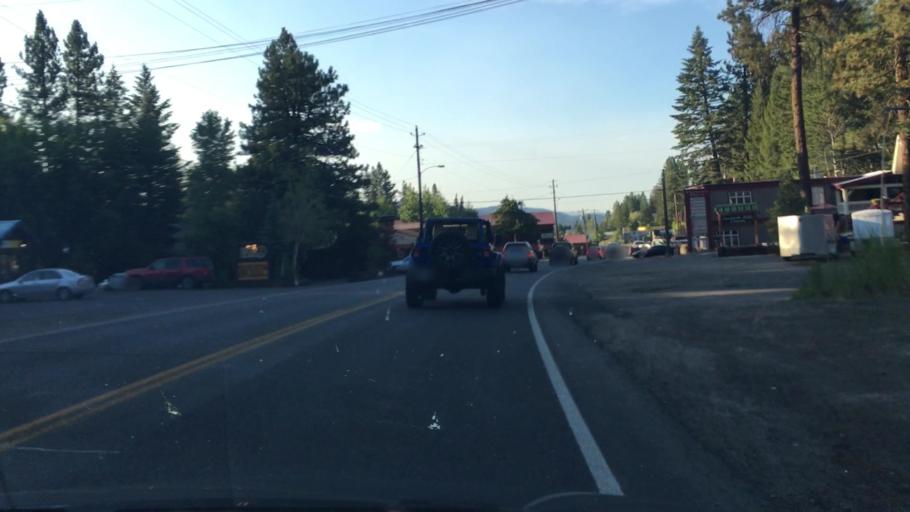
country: US
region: Idaho
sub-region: Valley County
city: McCall
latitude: 44.9033
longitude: -116.0983
